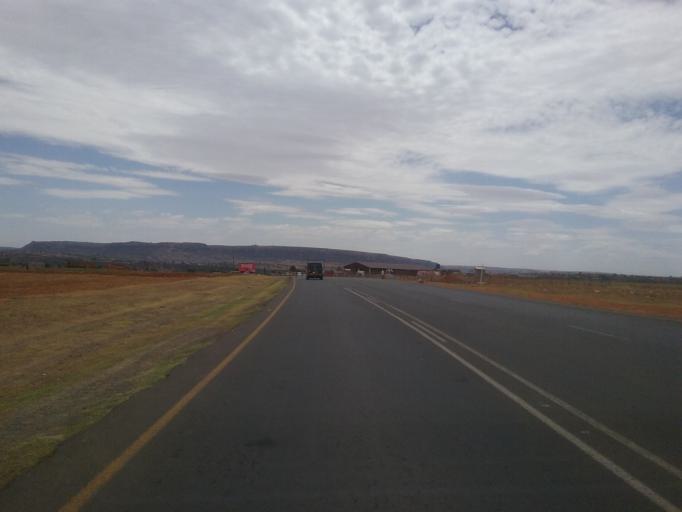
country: LS
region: Maseru
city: Maseru
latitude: -29.4282
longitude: 27.5613
